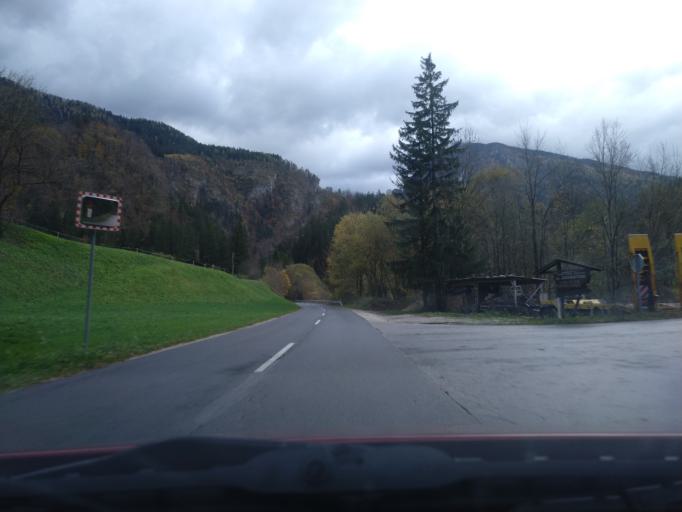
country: SI
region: Luce
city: Luce
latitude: 46.3626
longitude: 14.7345
